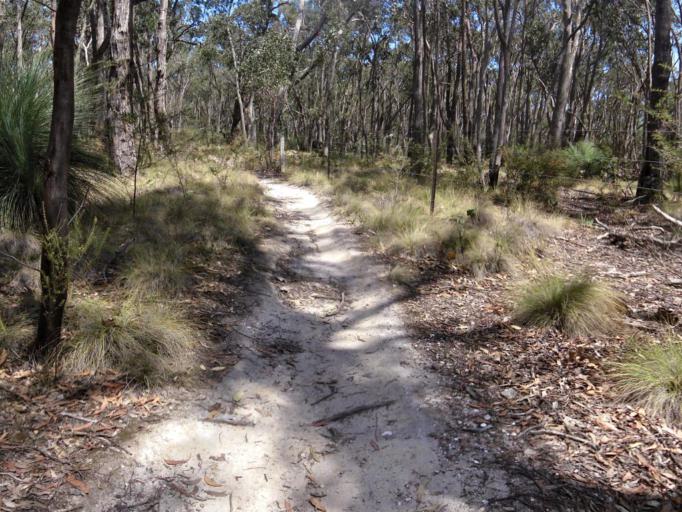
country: AU
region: Victoria
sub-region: Melton
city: Melton West
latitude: -37.5113
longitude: 144.5549
